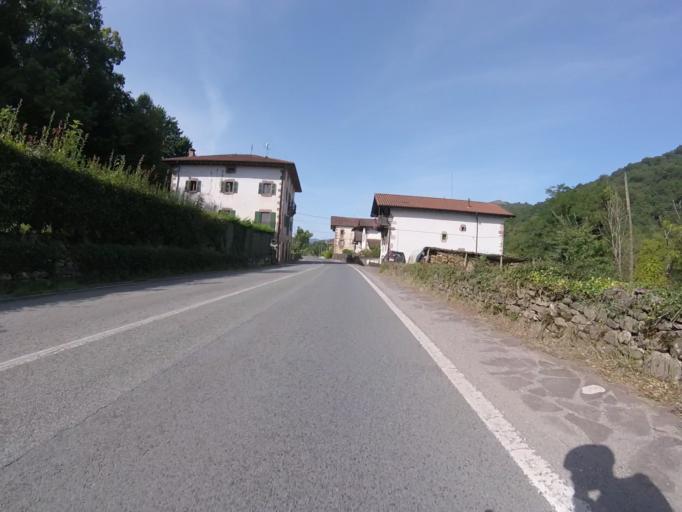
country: ES
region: Navarre
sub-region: Provincia de Navarra
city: Doneztebe
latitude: 43.1372
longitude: -1.6144
